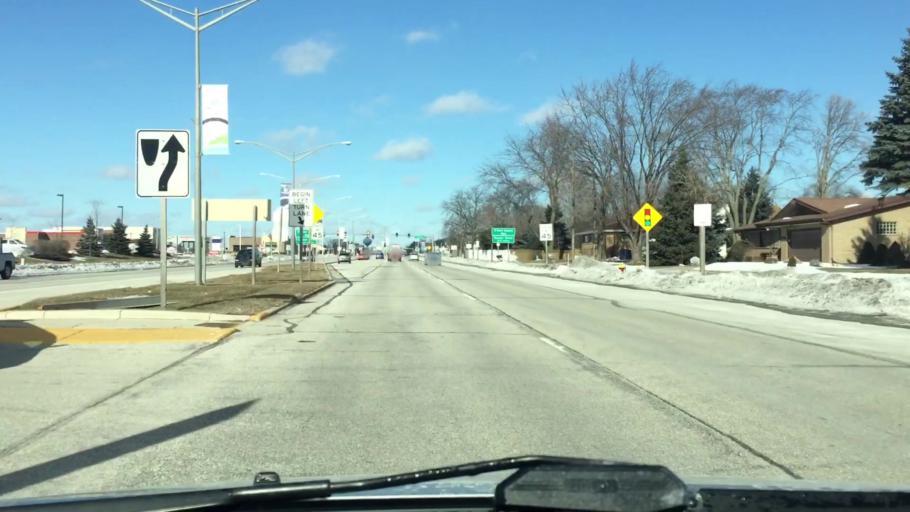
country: US
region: Wisconsin
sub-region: Milwaukee County
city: Oak Creek
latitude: 42.8957
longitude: -87.9117
